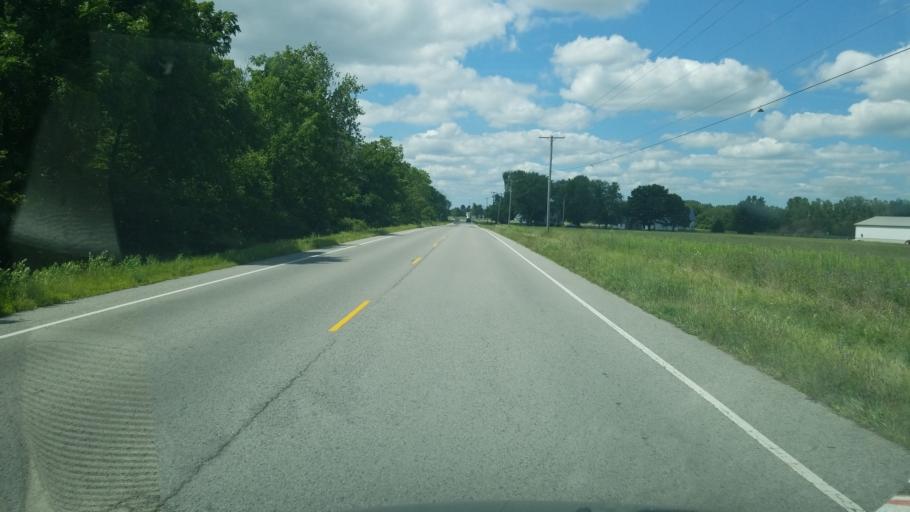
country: US
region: Ohio
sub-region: Henry County
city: Liberty Center
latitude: 41.4129
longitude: -84.0158
